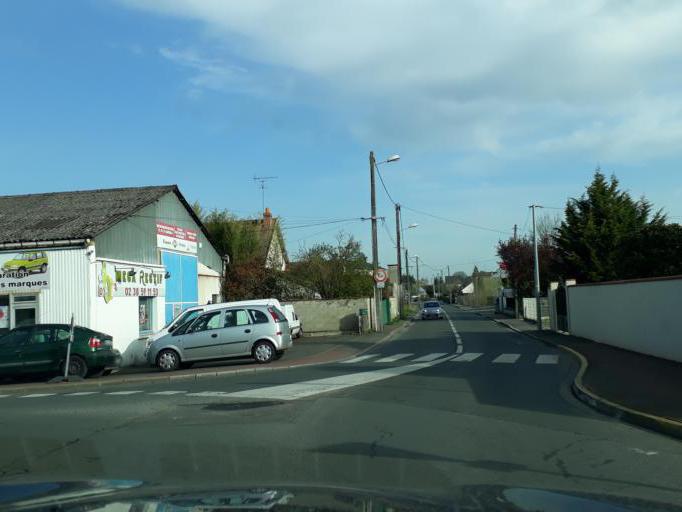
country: FR
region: Centre
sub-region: Departement du Loiret
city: La Chapelle-Saint-Mesmin
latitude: 47.8950
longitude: 1.8457
